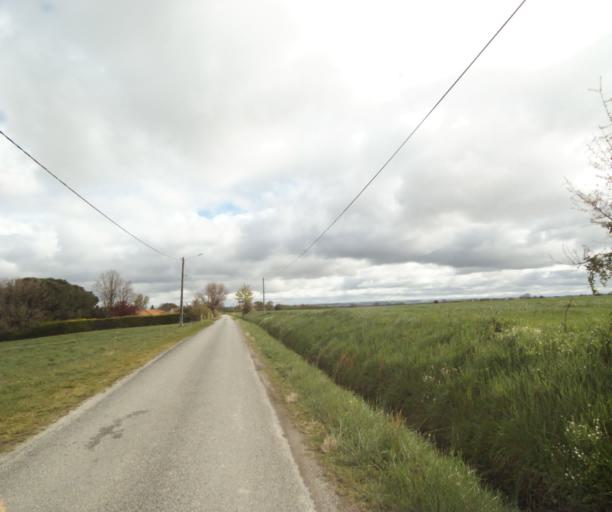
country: FR
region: Midi-Pyrenees
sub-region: Departement de l'Ariege
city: Saverdun
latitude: 43.2269
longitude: 1.5629
